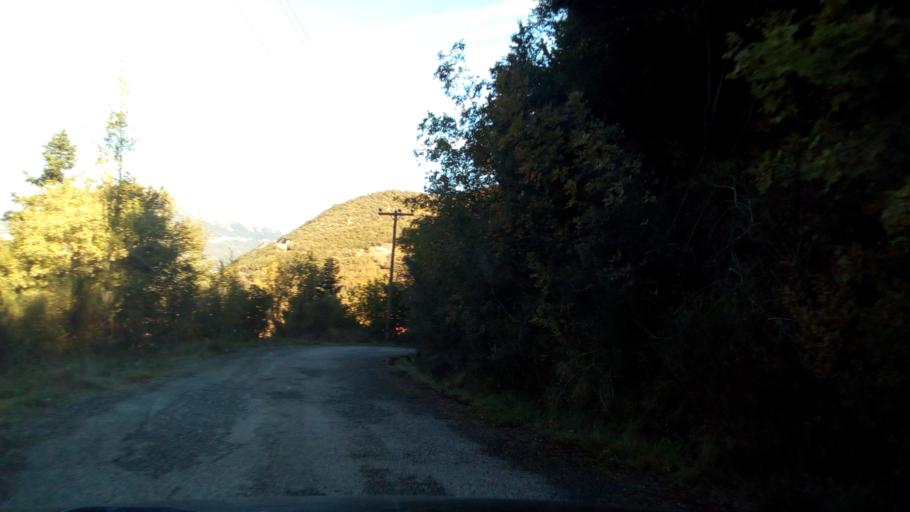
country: GR
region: West Greece
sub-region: Nomos Aitolias kai Akarnanias
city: Nafpaktos
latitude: 38.5602
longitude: 21.8525
